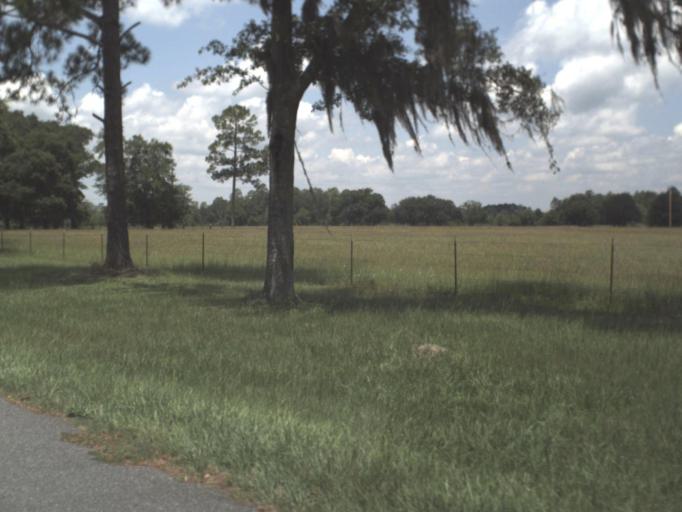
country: US
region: Florida
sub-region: Union County
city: Lake Butler
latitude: 30.0176
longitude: -82.4129
